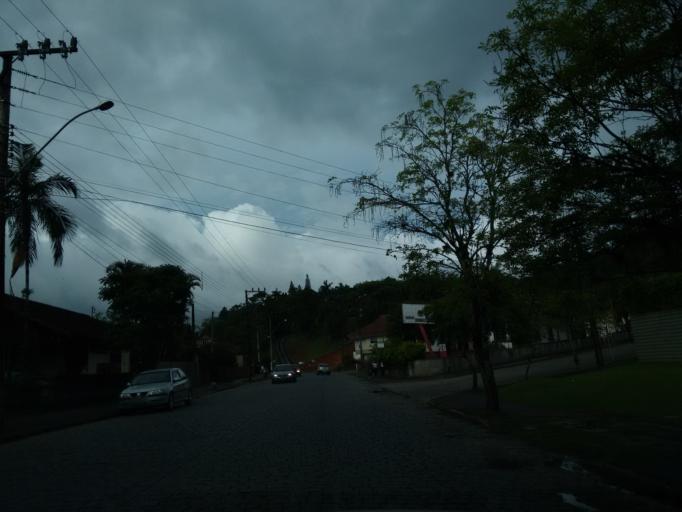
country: BR
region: Santa Catarina
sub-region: Pomerode
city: Pomerode
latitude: -26.7317
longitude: -49.1725
